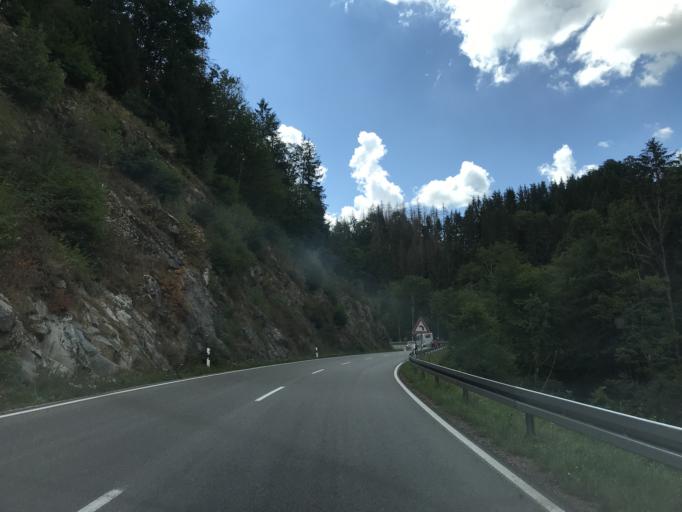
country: DE
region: Baden-Wuerttemberg
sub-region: Freiburg Region
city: Wembach
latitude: 47.7560
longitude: 7.8860
